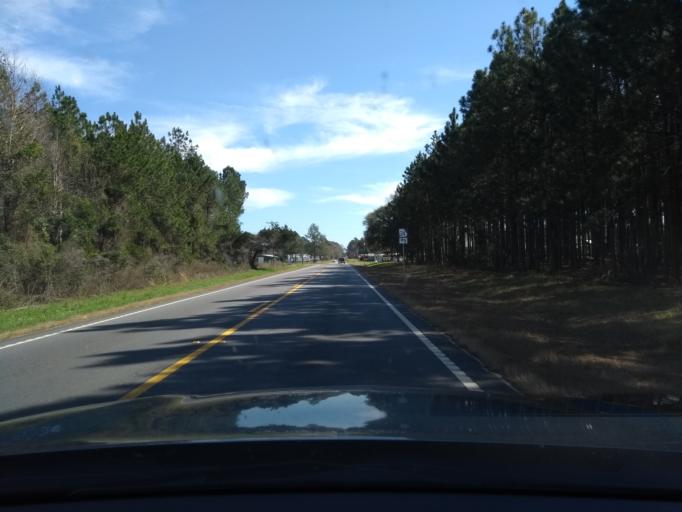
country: US
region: Georgia
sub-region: Bulloch County
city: Brooklet
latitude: 32.4736
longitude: -81.6078
